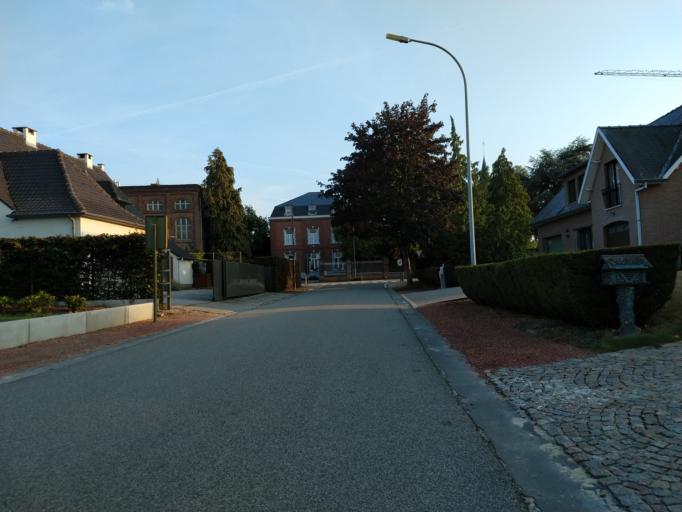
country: BE
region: Flanders
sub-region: Provincie Vlaams-Brabant
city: Hoegaarden
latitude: 50.7744
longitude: 4.8960
